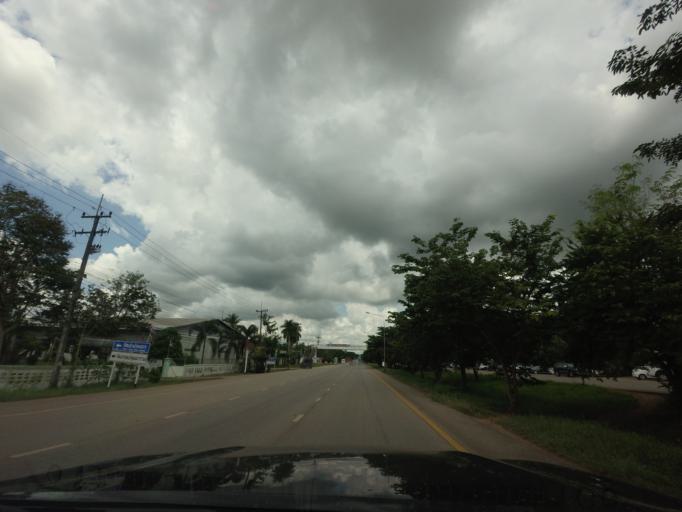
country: TH
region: Nong Khai
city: Sa Khrai
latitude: 17.5512
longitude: 102.8007
